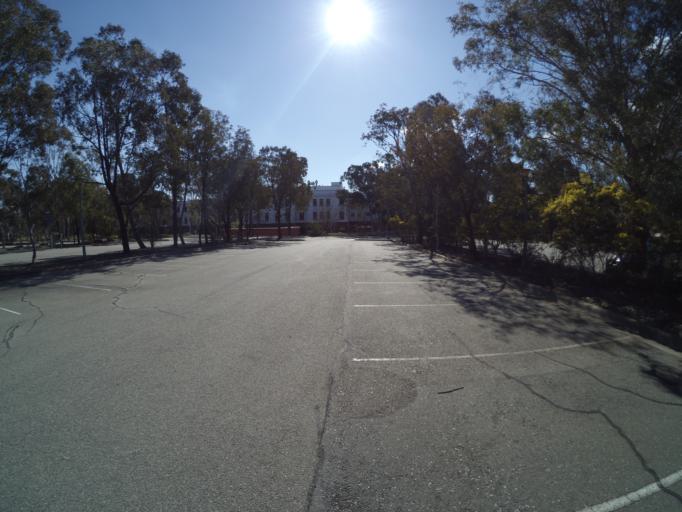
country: AU
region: Australian Capital Territory
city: Forrest
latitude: -35.3027
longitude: 149.1274
